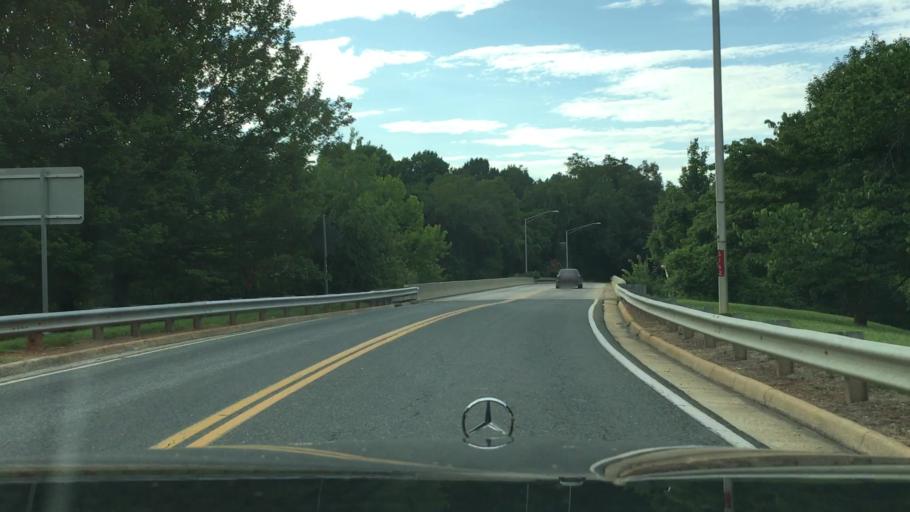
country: US
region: Virginia
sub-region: City of Lynchburg
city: West Lynchburg
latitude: 37.3858
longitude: -79.1670
